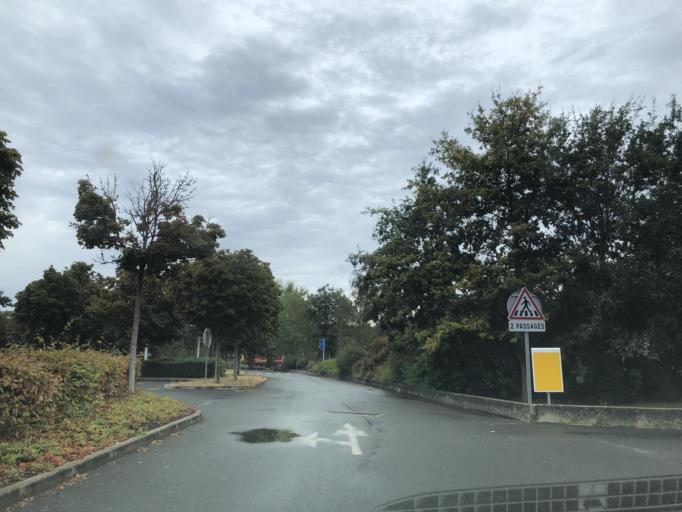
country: FR
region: Ile-de-France
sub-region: Departement de Seine-et-Marne
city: Montereau-Fault-Yonne
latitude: 48.4291
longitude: 2.9316
